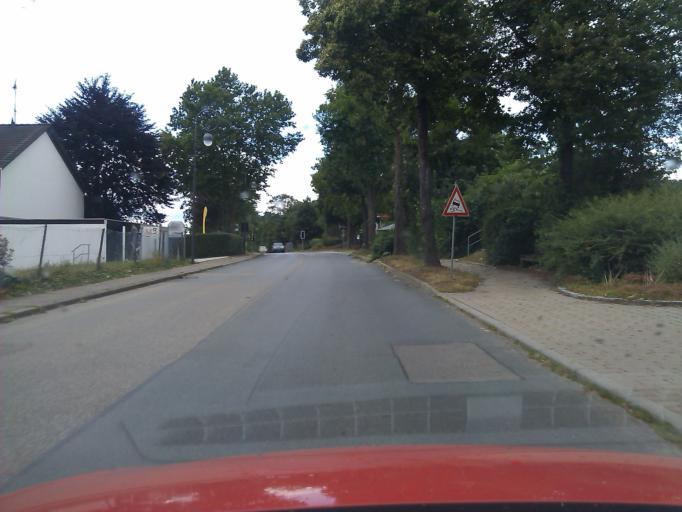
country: DE
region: Baden-Wuerttemberg
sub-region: Regierungsbezirk Stuttgart
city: Guglingen
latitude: 49.0671
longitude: 8.9943
